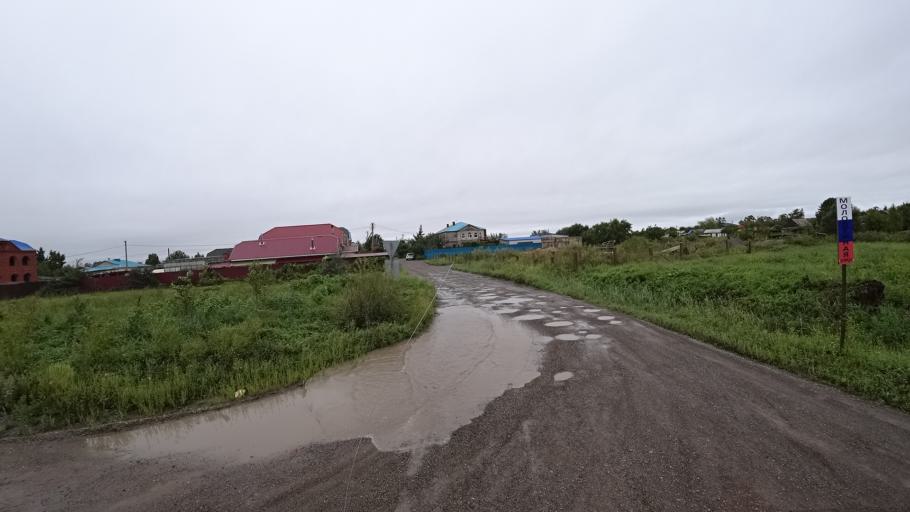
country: RU
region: Primorskiy
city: Monastyrishche
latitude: 44.2036
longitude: 132.4321
